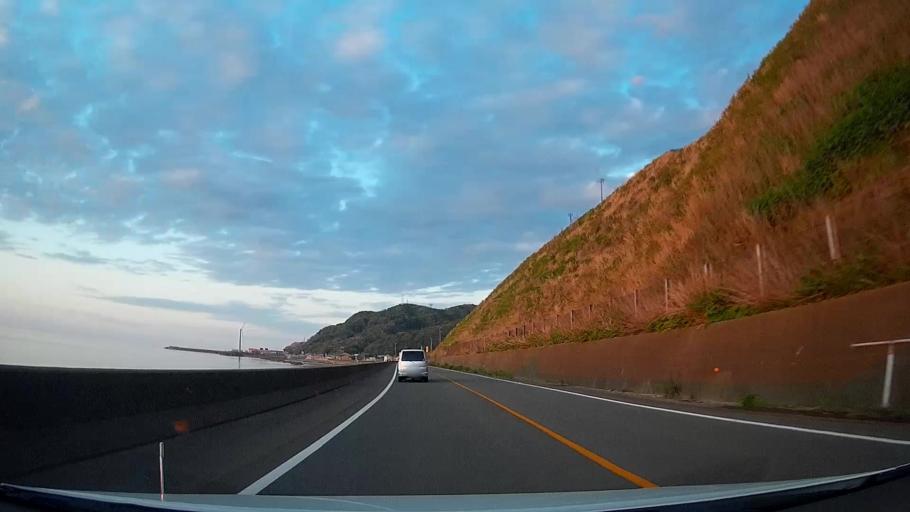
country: JP
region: Niigata
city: Joetsu
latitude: 37.1541
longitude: 138.0776
